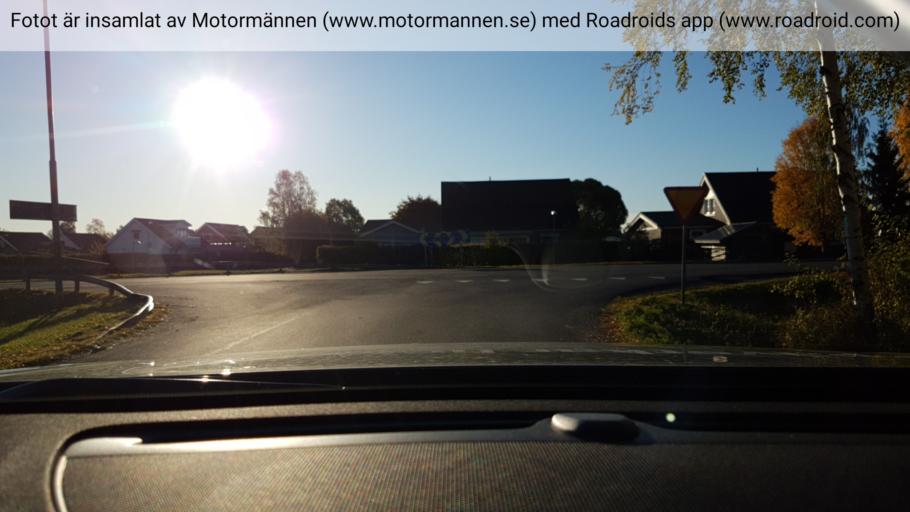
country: SE
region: Norrbotten
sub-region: Lulea Kommun
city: Sodra Sunderbyn
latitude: 65.6582
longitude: 21.9503
